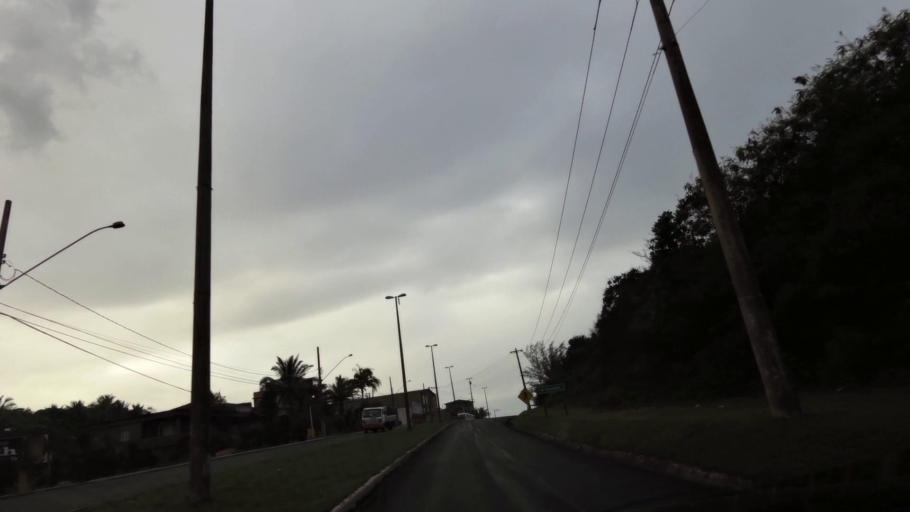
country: BR
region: Espirito Santo
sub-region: Guarapari
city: Guarapari
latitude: -20.7698
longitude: -40.5750
